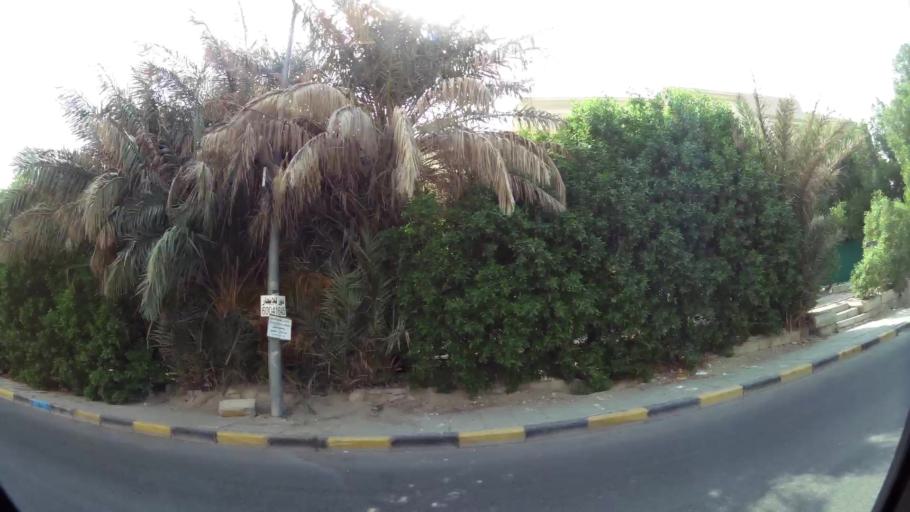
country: KW
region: Muhafazat al Jahra'
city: Al Jahra'
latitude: 29.3191
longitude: 47.6719
